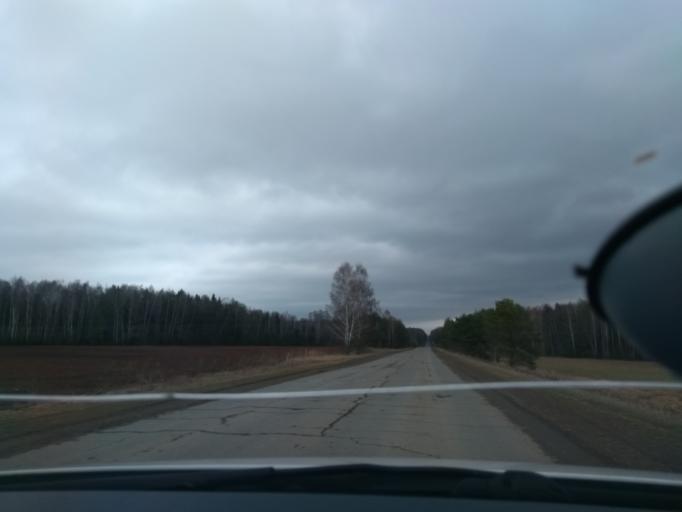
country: RU
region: Perm
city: Kungur
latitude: 57.3475
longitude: 56.7938
